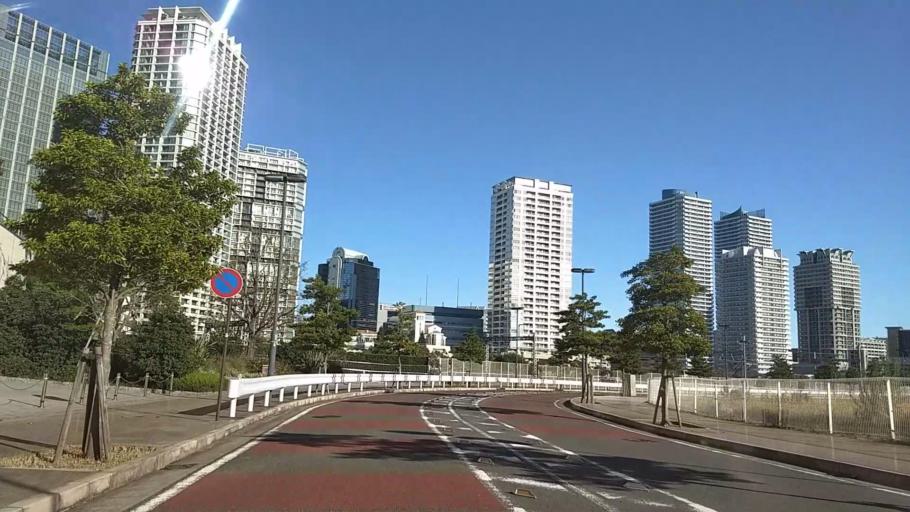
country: JP
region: Kanagawa
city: Yokohama
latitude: 35.4642
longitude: 139.6285
